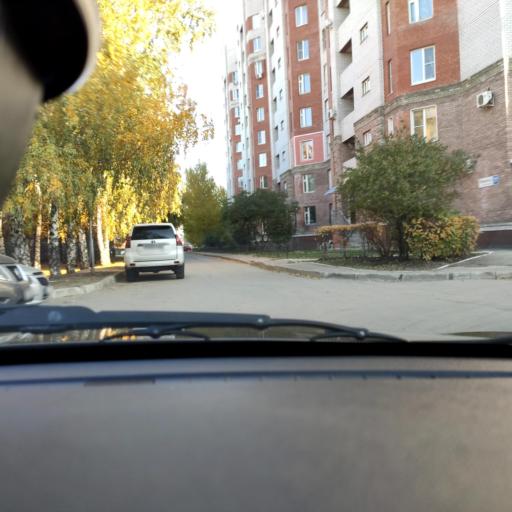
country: RU
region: Samara
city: Tol'yatti
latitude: 53.5494
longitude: 49.3252
